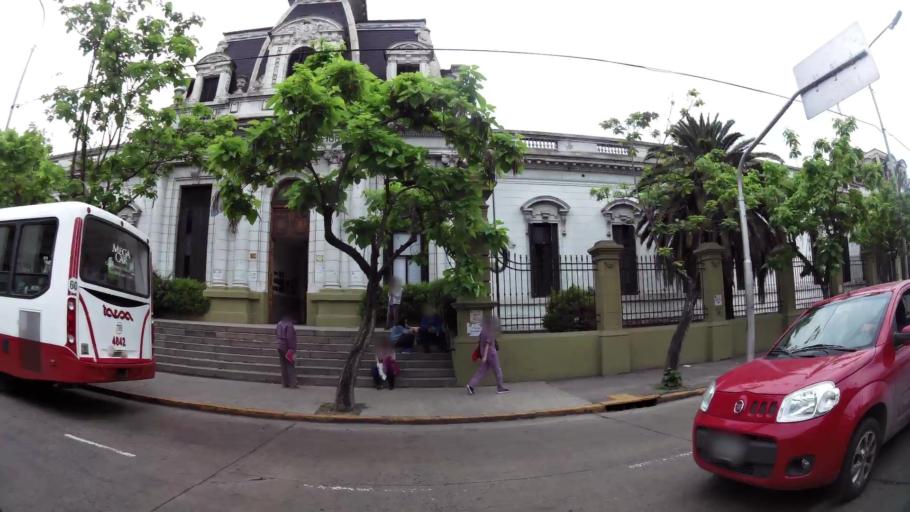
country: AR
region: Buenos Aires
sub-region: Partido de Avellaneda
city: Avellaneda
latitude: -34.6662
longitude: -58.3653
